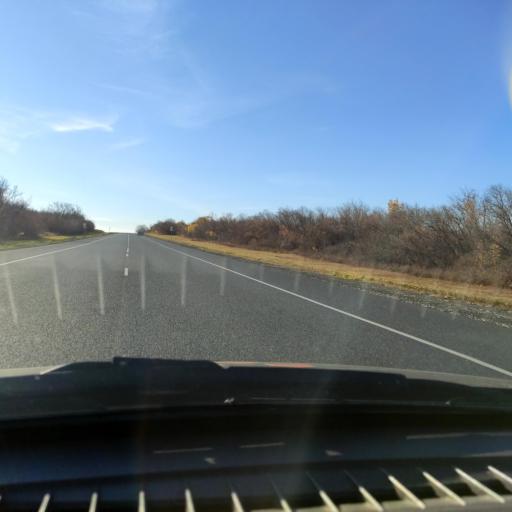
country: RU
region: Samara
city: Mezhdurechensk
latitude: 53.2549
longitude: 49.0471
